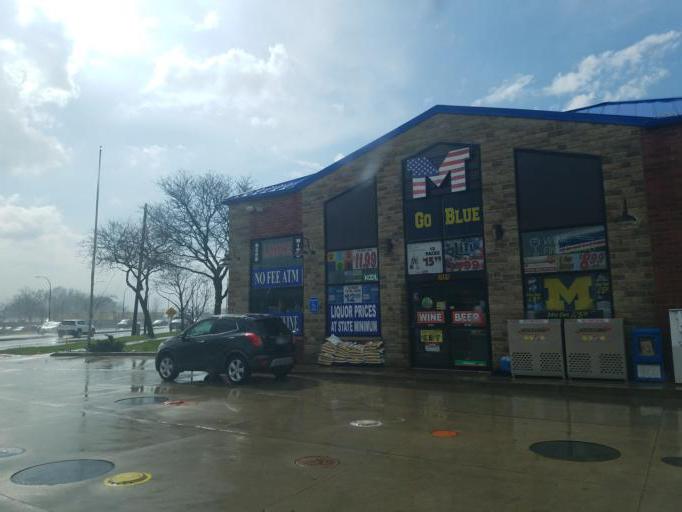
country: US
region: Michigan
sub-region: Washtenaw County
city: Ann Arbor
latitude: 42.2556
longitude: -83.6884
